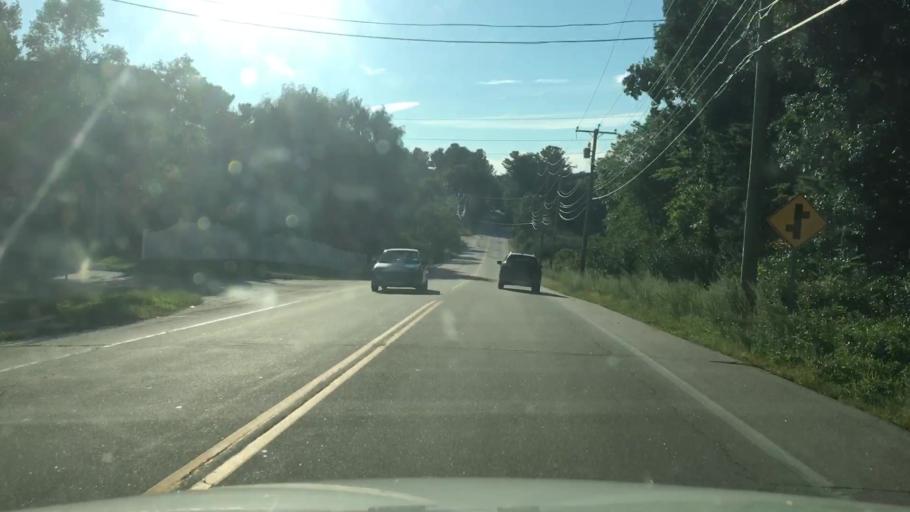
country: US
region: New Hampshire
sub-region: Strafford County
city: Dover
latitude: 43.1666
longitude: -70.8479
